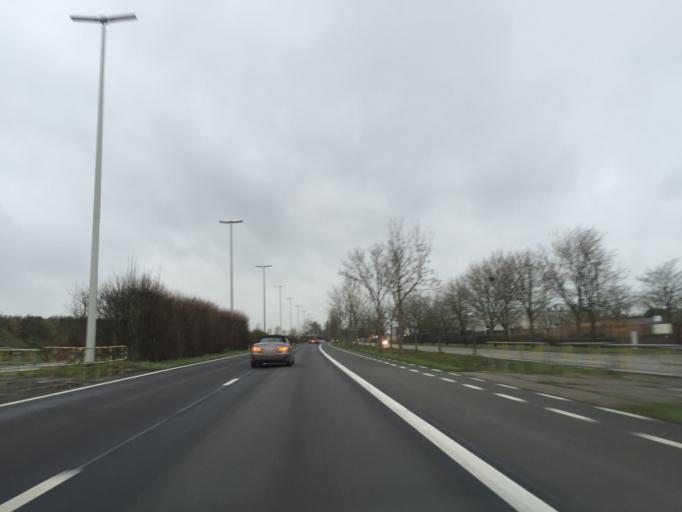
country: BE
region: Flanders
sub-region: Provincie Oost-Vlaanderen
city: Evergem
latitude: 51.0953
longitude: 3.7040
